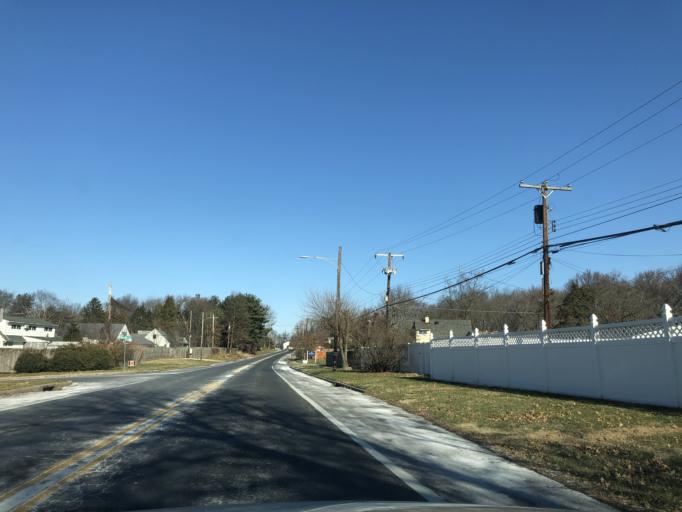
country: US
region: Pennsylvania
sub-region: Bucks County
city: Fairless Hills
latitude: 40.1577
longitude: -74.8758
